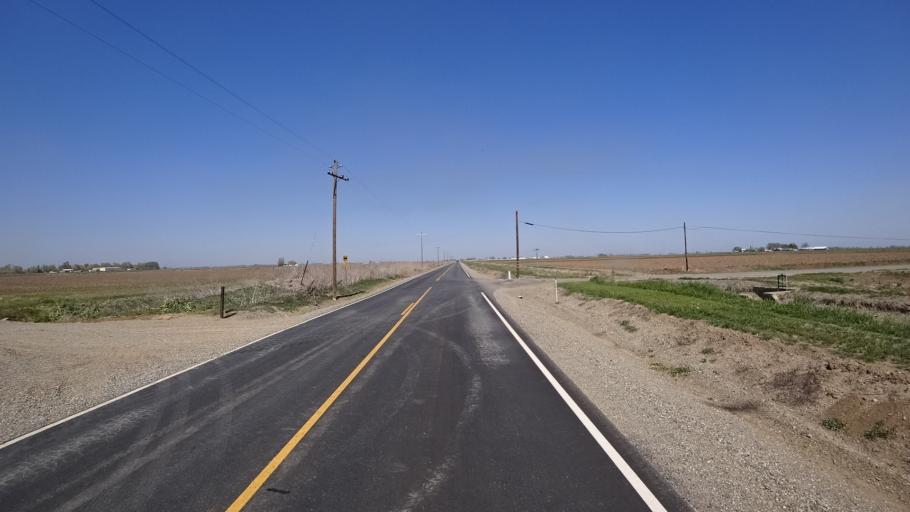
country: US
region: California
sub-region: Glenn County
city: Willows
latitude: 39.4874
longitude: -122.1367
